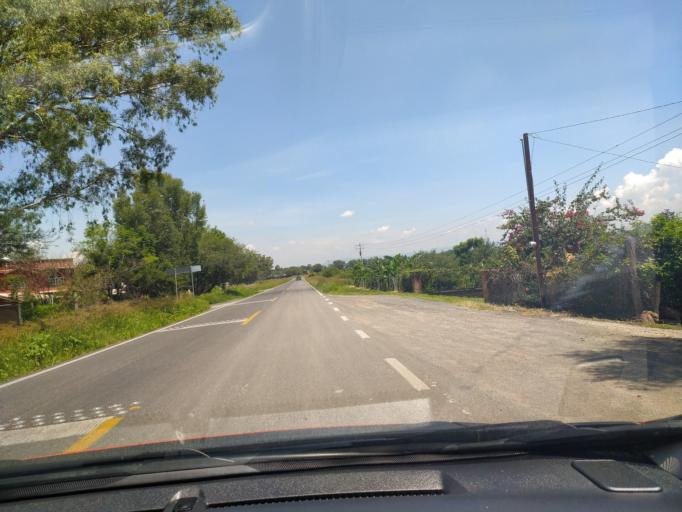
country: MX
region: Guanajuato
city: Ciudad Manuel Doblado
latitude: 20.8000
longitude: -101.9886
